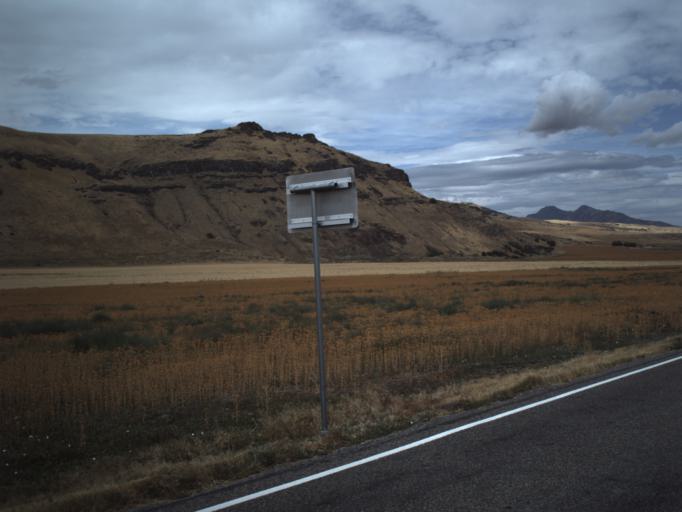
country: US
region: Utah
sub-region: Cache County
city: Benson
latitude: 41.7893
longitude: -111.9882
